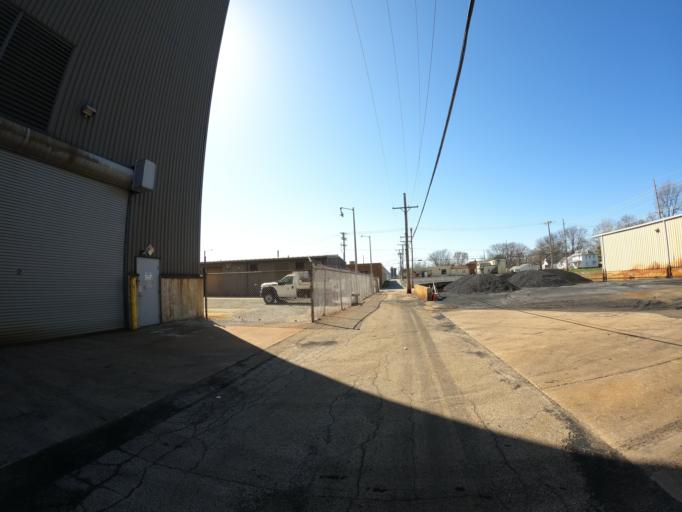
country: US
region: Illinois
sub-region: Sangamon County
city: Springfield
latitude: 39.8047
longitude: -89.6569
